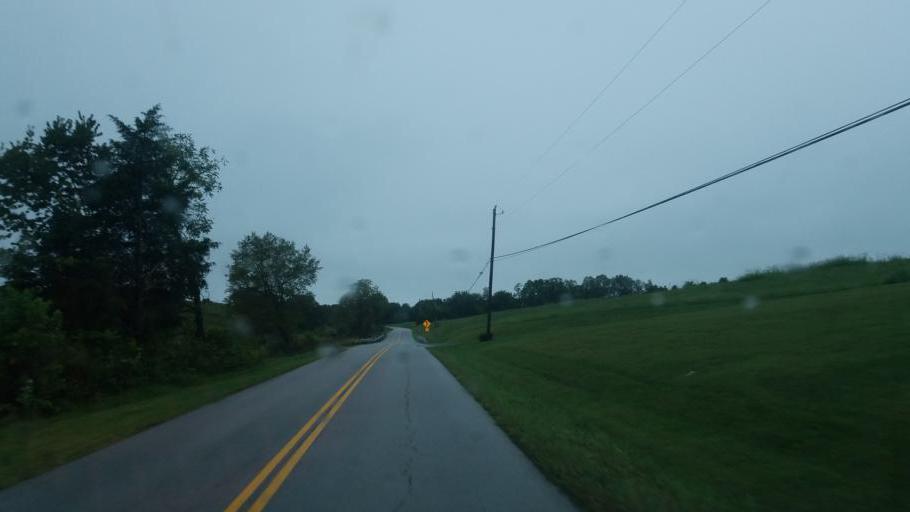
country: US
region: Kentucky
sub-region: Fleming County
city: Flemingsburg
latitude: 38.4229
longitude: -83.7049
